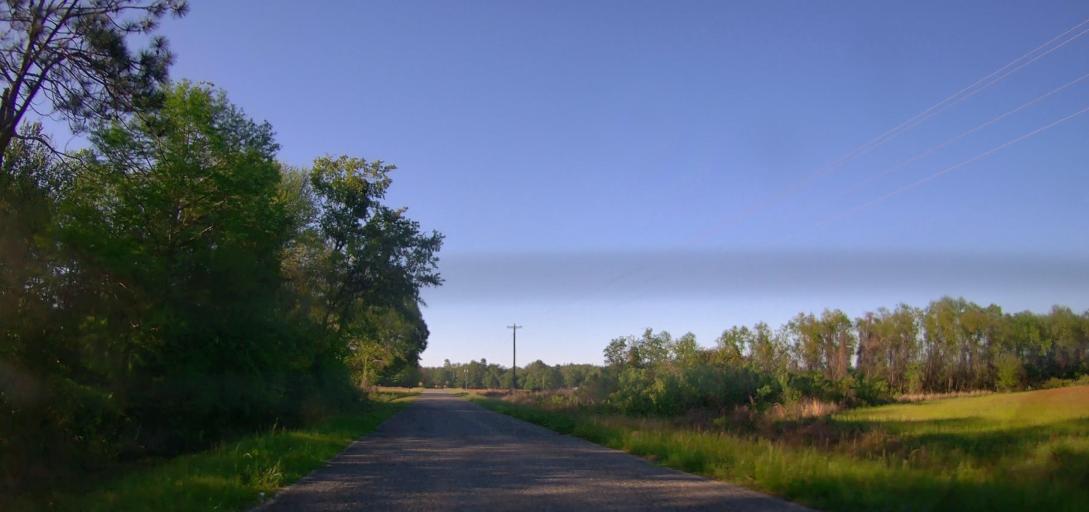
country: US
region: Georgia
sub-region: Ben Hill County
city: Fitzgerald
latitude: 31.6998
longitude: -83.1531
